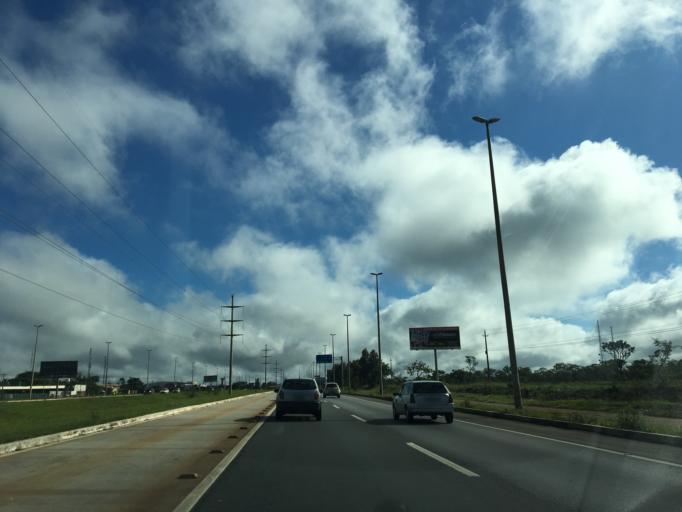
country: BR
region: Federal District
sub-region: Brasilia
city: Brasilia
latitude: -15.9735
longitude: -48.0287
